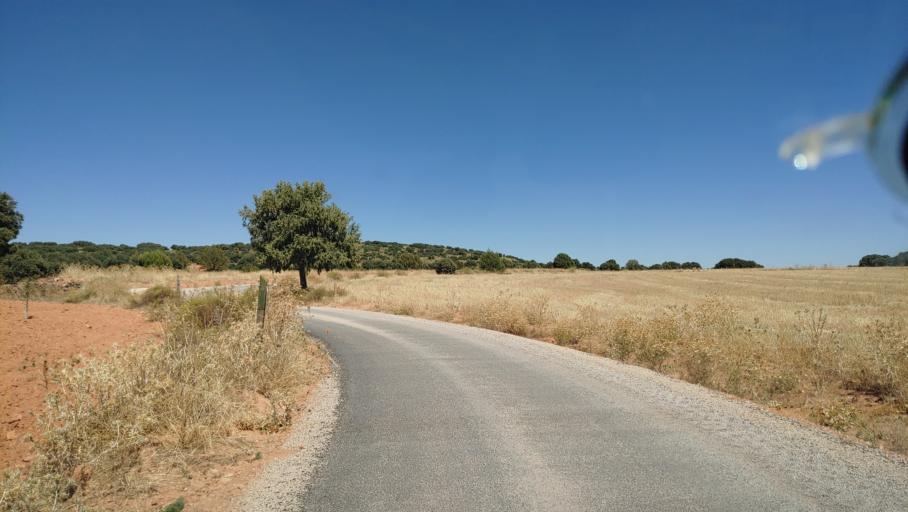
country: ES
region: Castille-La Mancha
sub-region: Provincia de Albacete
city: Ossa de Montiel
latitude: 38.9297
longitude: -2.7775
